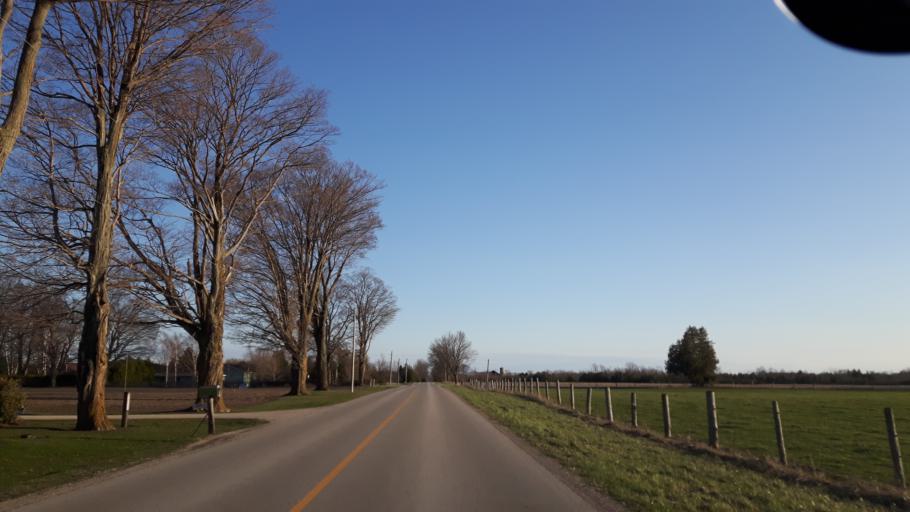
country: CA
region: Ontario
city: Goderich
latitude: 43.6627
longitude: -81.6847
